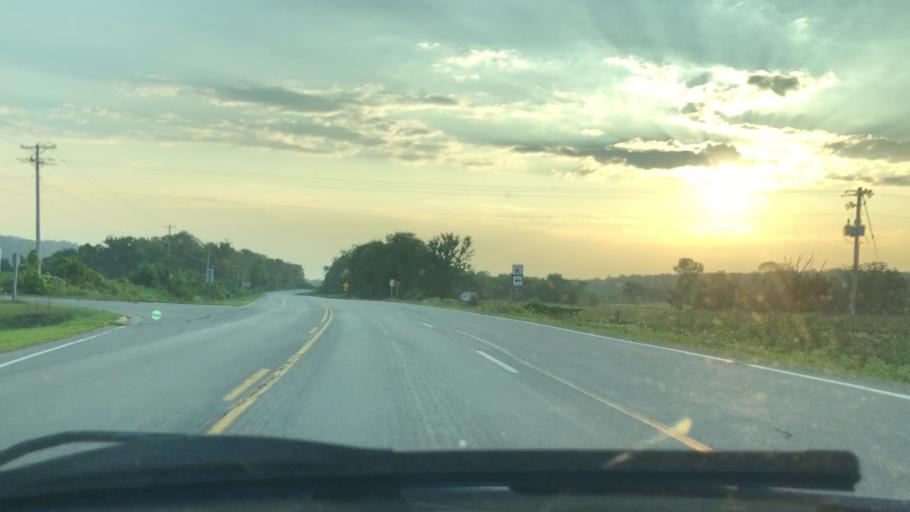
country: US
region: Wisconsin
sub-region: Dane County
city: Mazomanie
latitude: 43.1620
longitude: -89.8473
